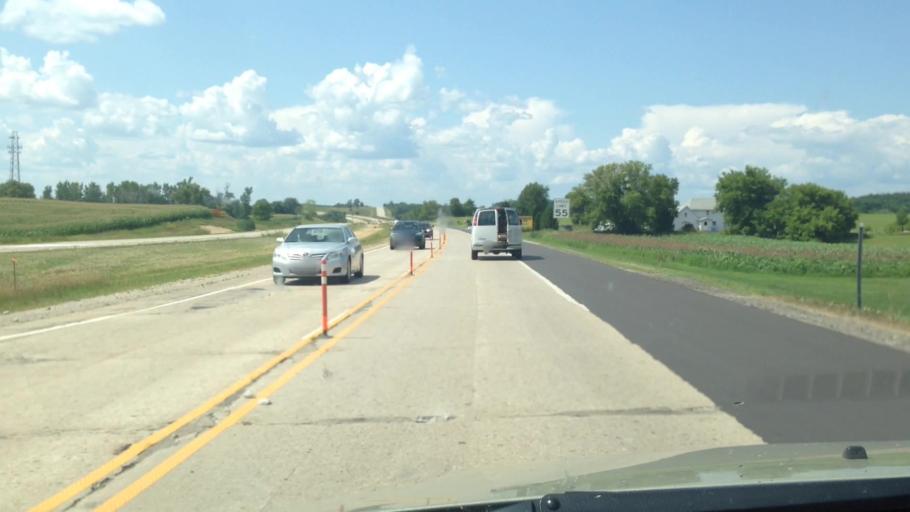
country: US
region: Wisconsin
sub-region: Shawano County
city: Bonduel
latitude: 44.7119
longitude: -88.3839
